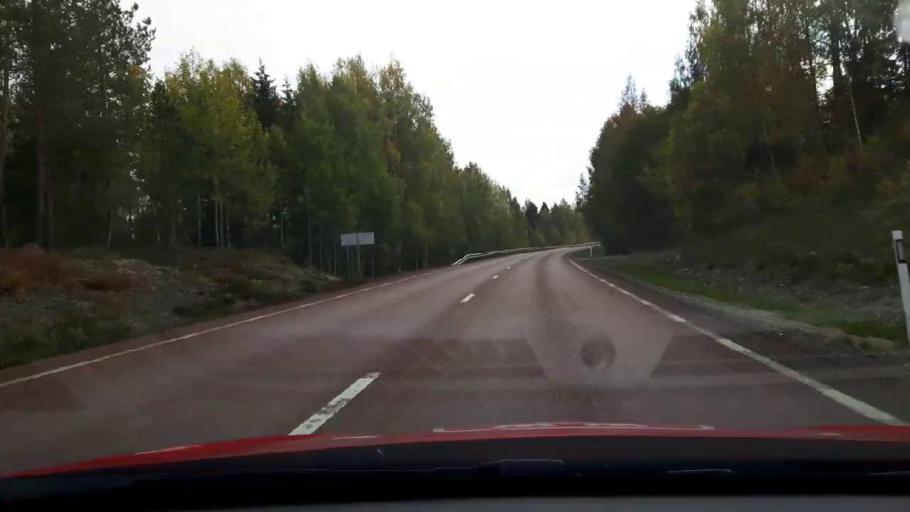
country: SE
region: Gaevleborg
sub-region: Ljusdals Kommun
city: Jaervsoe
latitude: 61.6356
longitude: 16.2648
